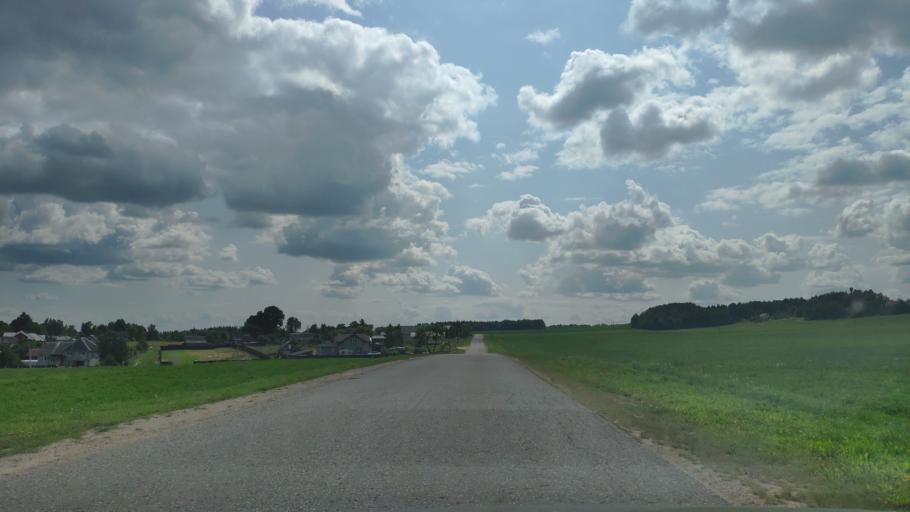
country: BY
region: Minsk
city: Khatsyezhyna
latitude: 53.8602
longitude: 27.3100
